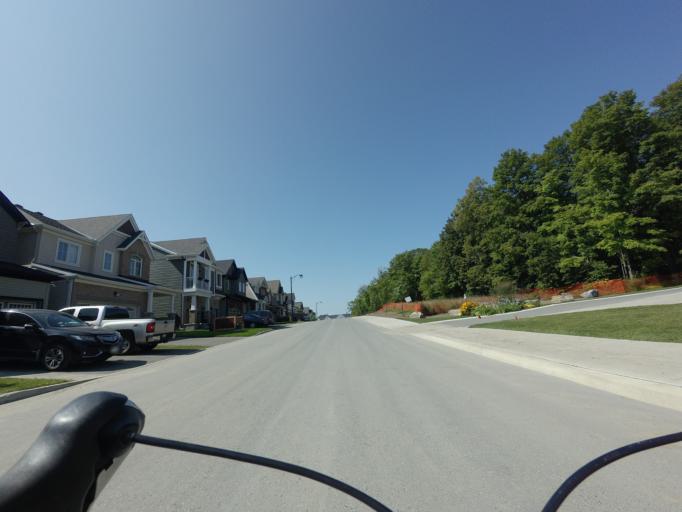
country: CA
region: Ontario
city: Bells Corners
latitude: 45.2786
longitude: -75.8399
